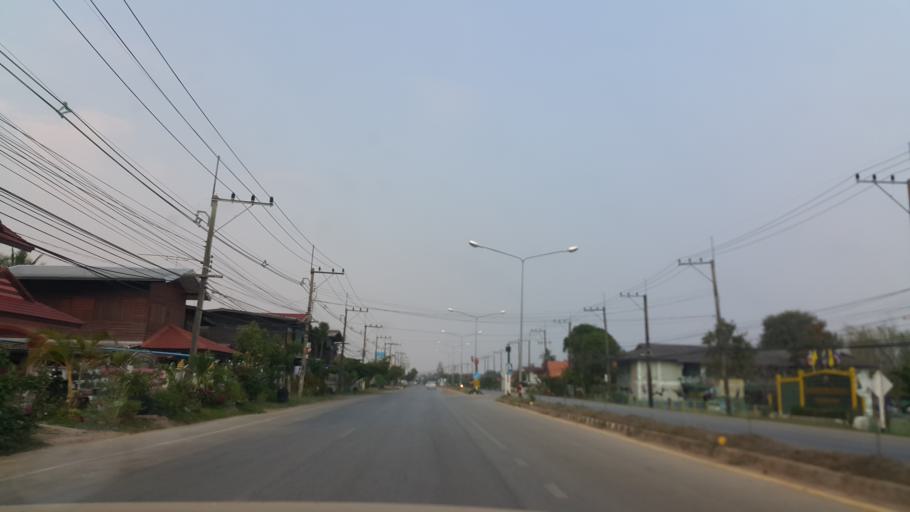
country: TH
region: Nakhon Phanom
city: That Phanom
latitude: 16.9743
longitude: 104.7273
